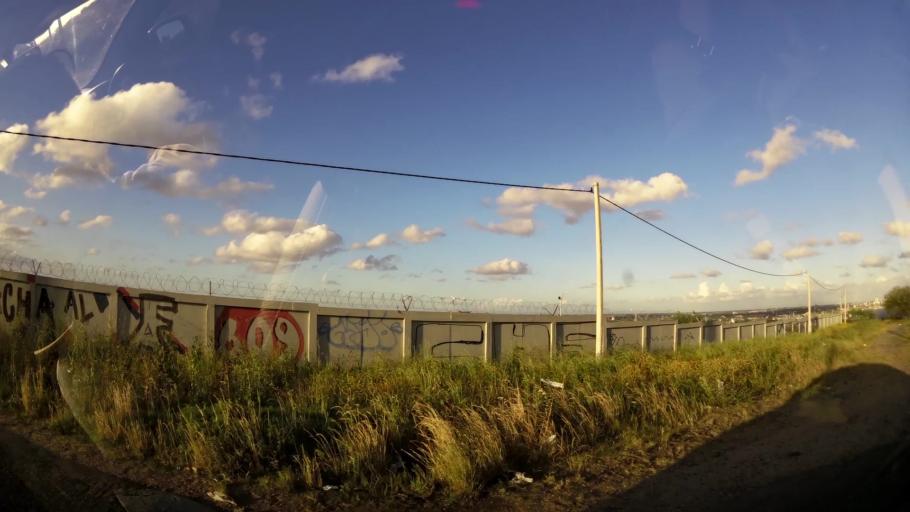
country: UY
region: Montevideo
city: Montevideo
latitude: -34.8863
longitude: -56.2587
